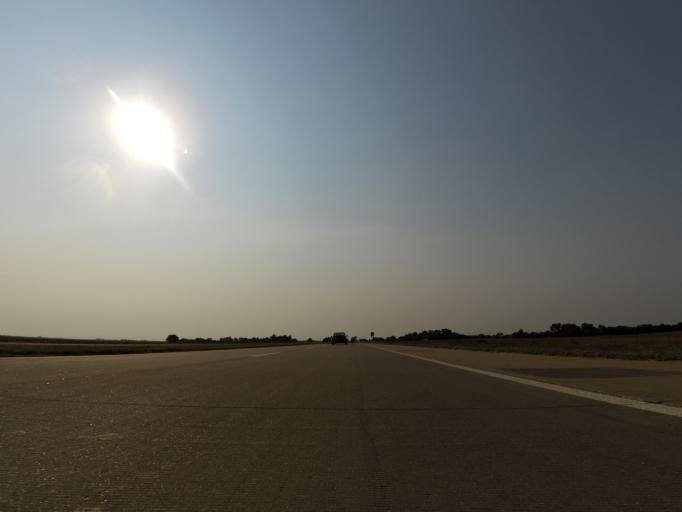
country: US
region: Kansas
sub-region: Sedgwick County
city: Colwich
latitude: 37.8513
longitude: -97.6013
